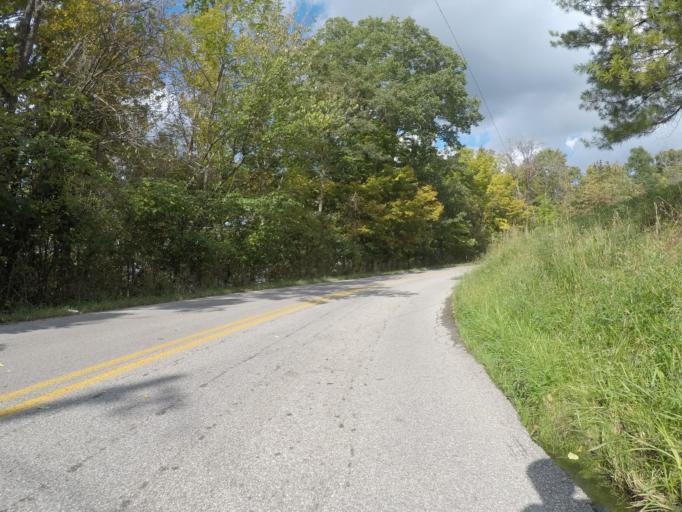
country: US
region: West Virginia
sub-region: Cabell County
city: Huntington
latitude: 38.4011
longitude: -82.4382
